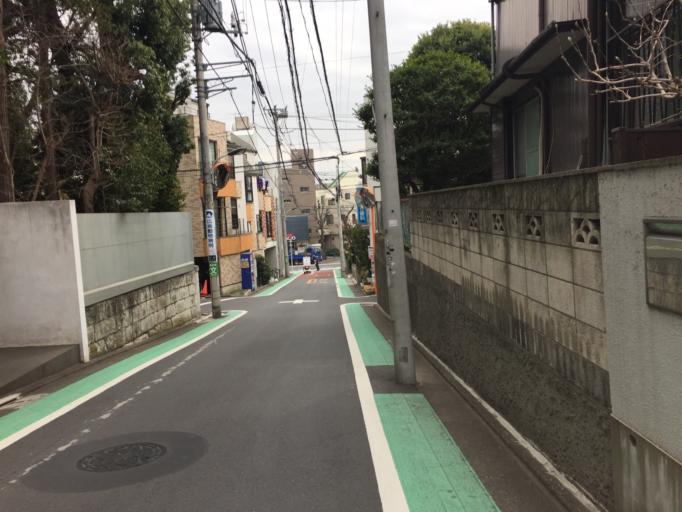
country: JP
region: Tokyo
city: Tokyo
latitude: 35.6554
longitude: 139.6732
